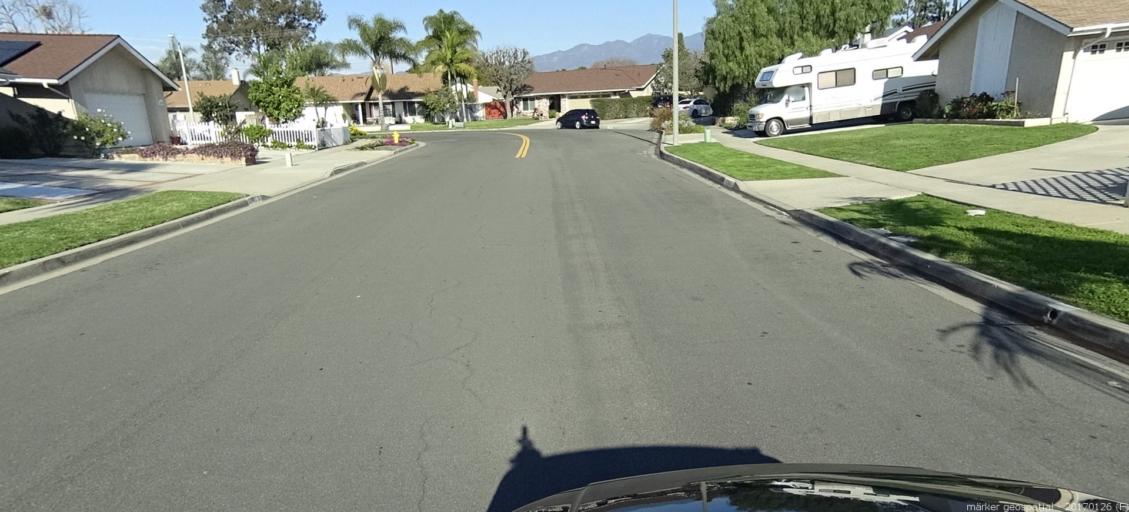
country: US
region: California
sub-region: Orange County
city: Lake Forest
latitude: 33.6334
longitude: -117.6883
